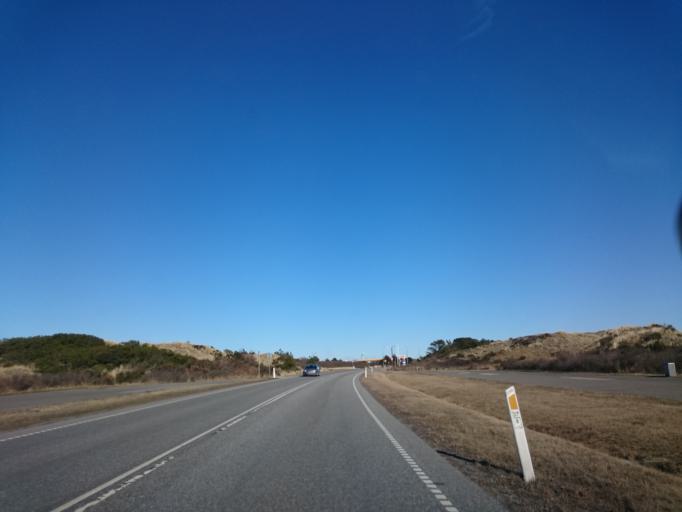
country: DK
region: North Denmark
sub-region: Frederikshavn Kommune
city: Skagen
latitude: 57.7249
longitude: 10.5445
